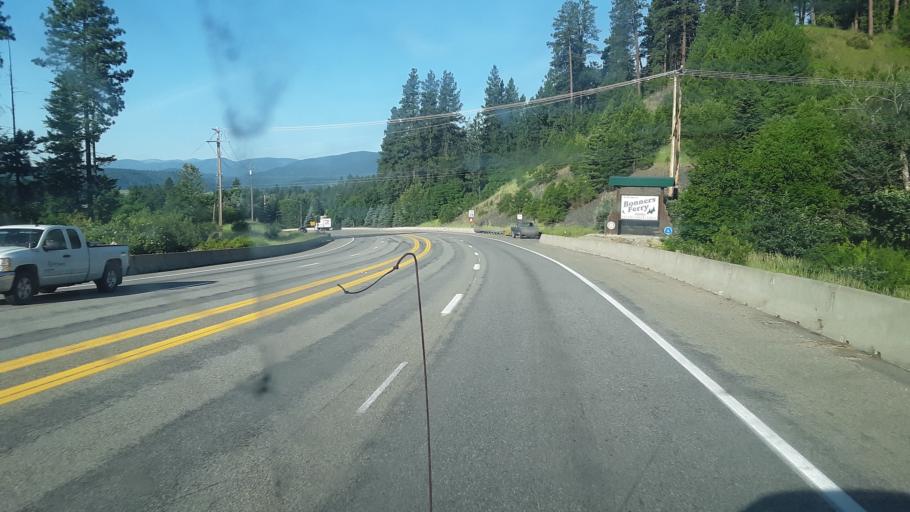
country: US
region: Idaho
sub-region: Boundary County
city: Bonners Ferry
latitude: 48.7092
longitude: -116.3076
